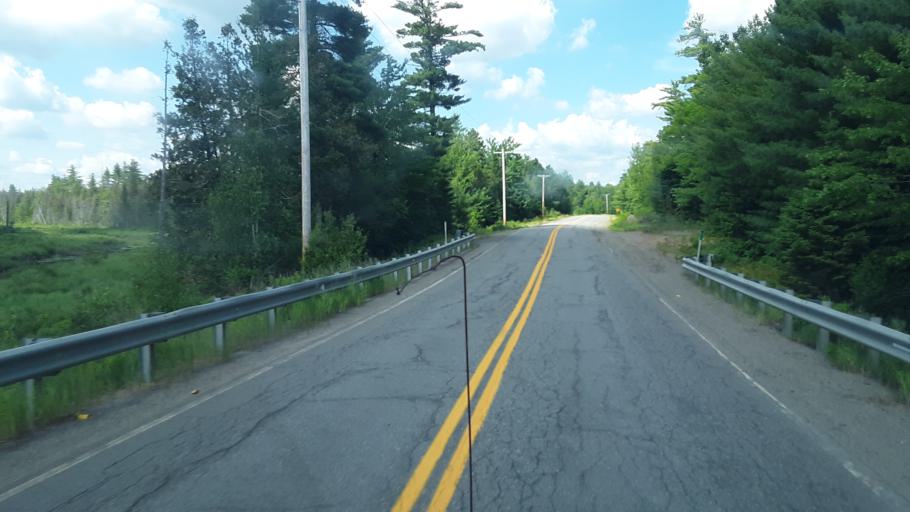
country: US
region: Maine
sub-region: Washington County
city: Calais
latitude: 45.1245
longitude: -67.4975
